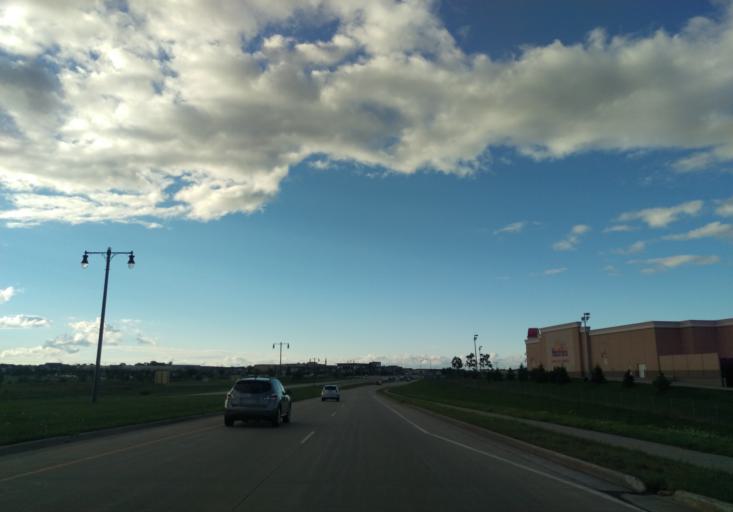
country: US
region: Wisconsin
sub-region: Dane County
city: Sun Prairie
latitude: 43.1629
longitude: -89.2680
